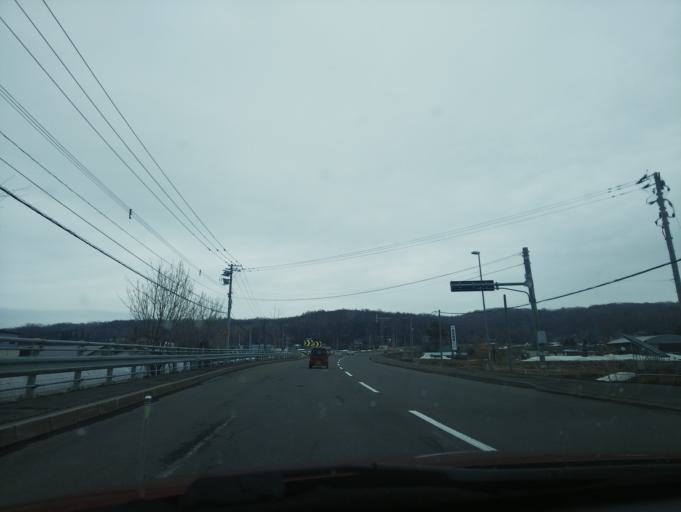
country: JP
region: Hokkaido
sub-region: Asahikawa-shi
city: Asahikawa
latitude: 43.8459
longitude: 142.4451
